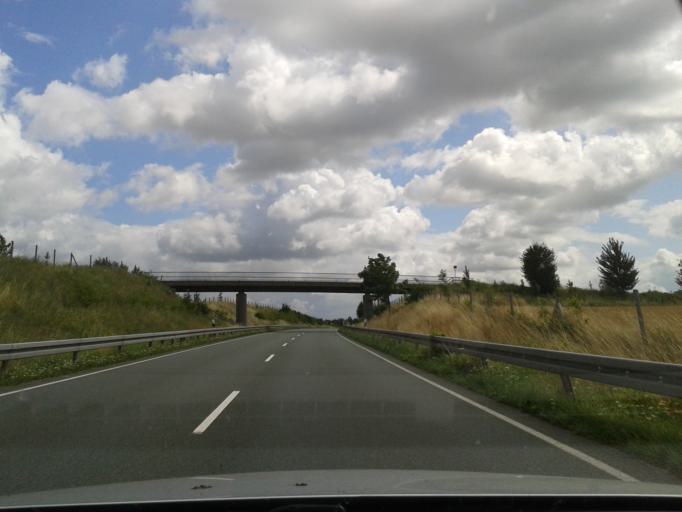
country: DE
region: North Rhine-Westphalia
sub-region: Regierungsbezirk Detmold
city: Lemgo
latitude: 51.9971
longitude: 8.9050
